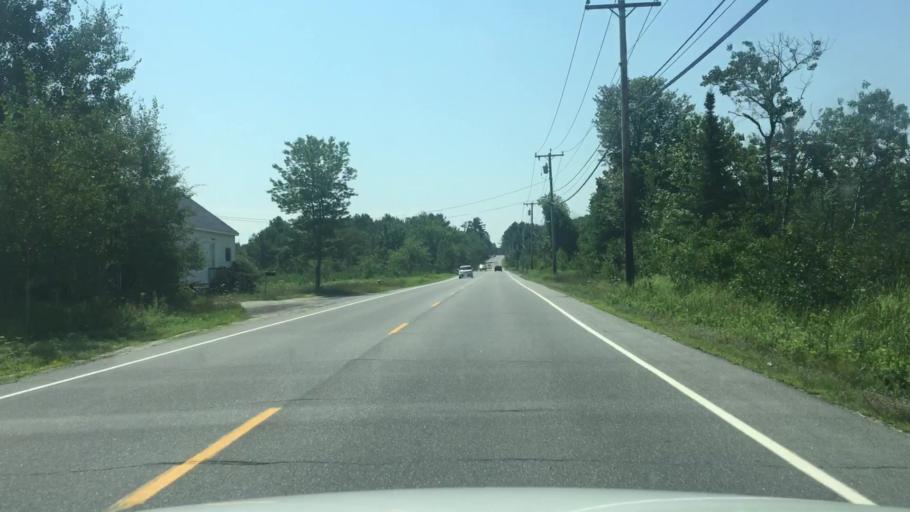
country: US
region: Maine
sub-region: Cumberland County
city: Cumberland Center
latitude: 43.8697
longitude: -70.3256
